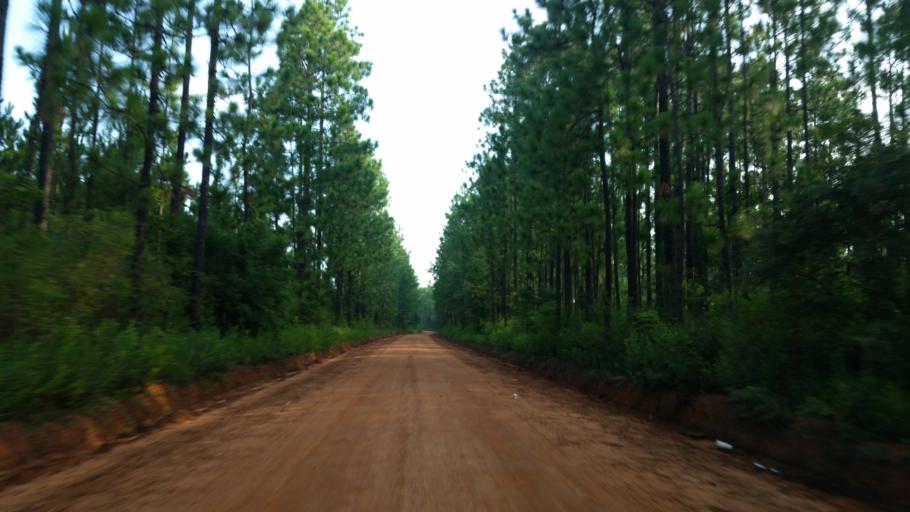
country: US
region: Alabama
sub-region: Escambia County
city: Atmore
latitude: 30.9400
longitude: -87.5718
